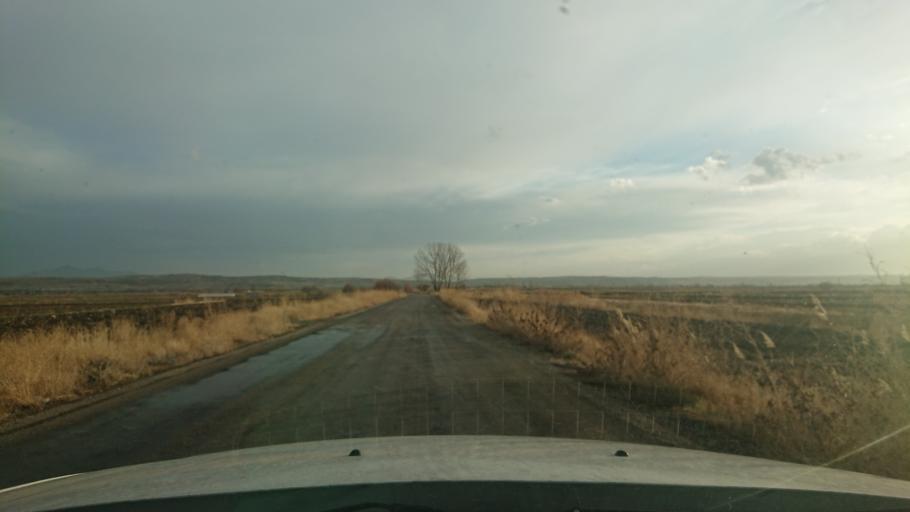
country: TR
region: Aksaray
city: Acipinar
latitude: 38.4730
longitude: 33.8548
